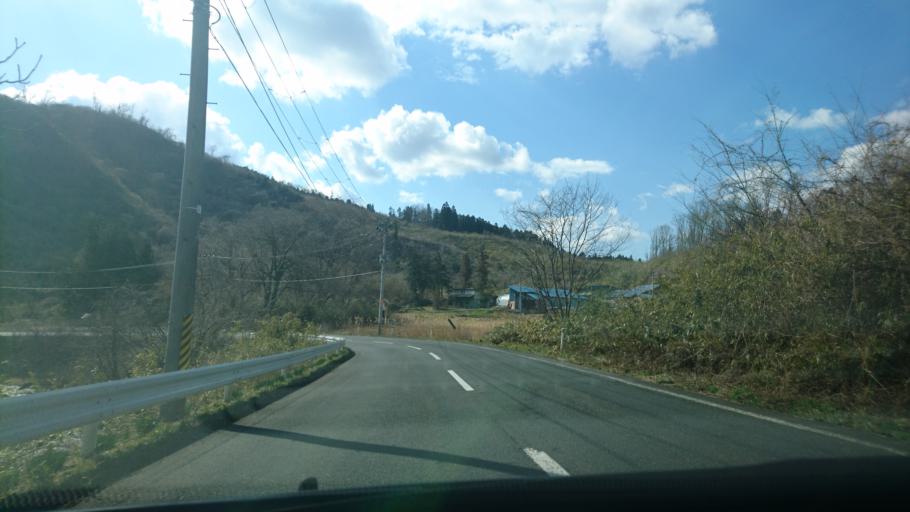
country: JP
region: Iwate
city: Kitakami
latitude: 39.2660
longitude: 141.2164
